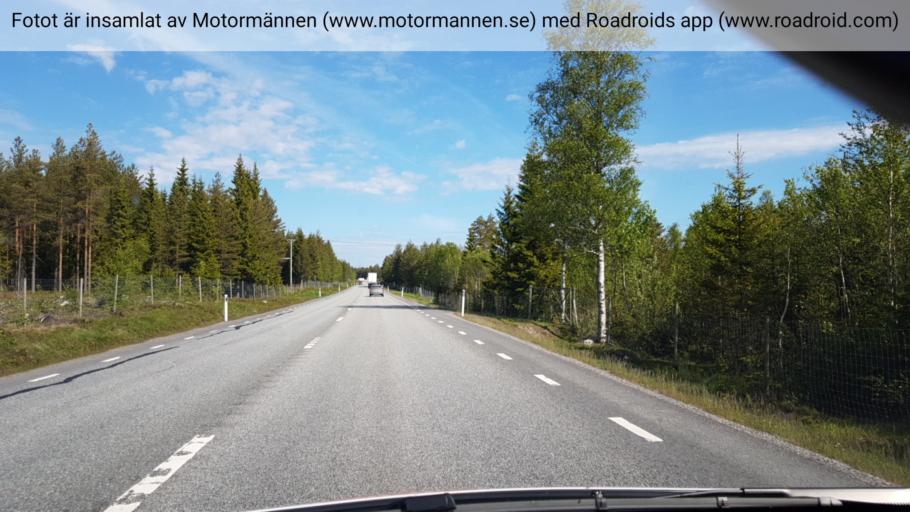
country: SE
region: Vaesterbotten
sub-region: Skelleftea Kommun
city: Burea
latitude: 64.4701
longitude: 21.2926
